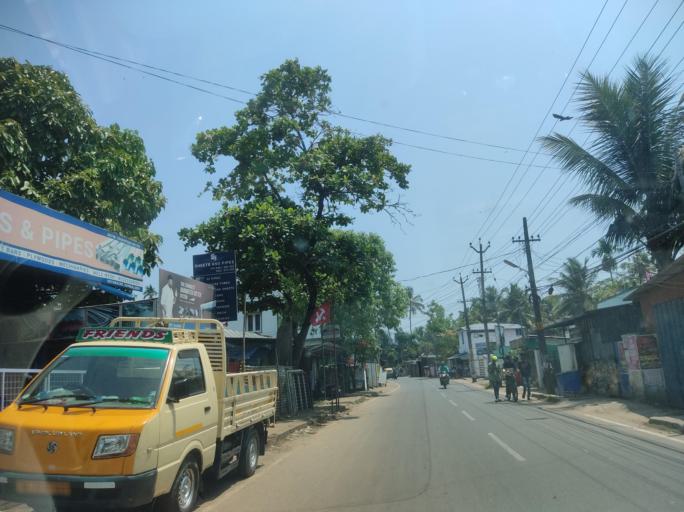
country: IN
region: Kerala
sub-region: Ernakulam
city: Cochin
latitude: 9.8931
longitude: 76.2847
